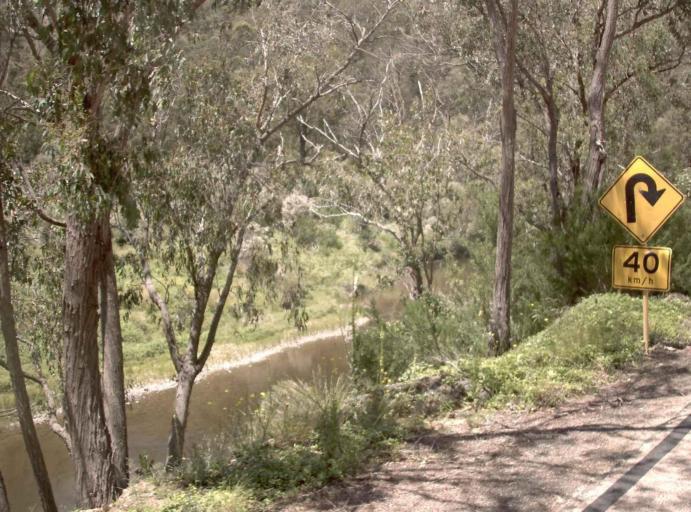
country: AU
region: Victoria
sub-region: East Gippsland
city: Bairnsdale
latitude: -37.4658
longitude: 147.8322
